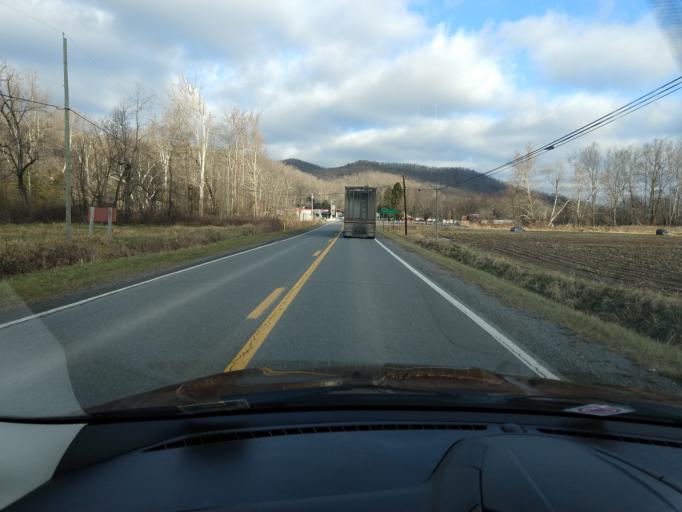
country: US
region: West Virginia
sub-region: Randolph County
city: Elkins
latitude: 38.7079
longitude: -79.9783
